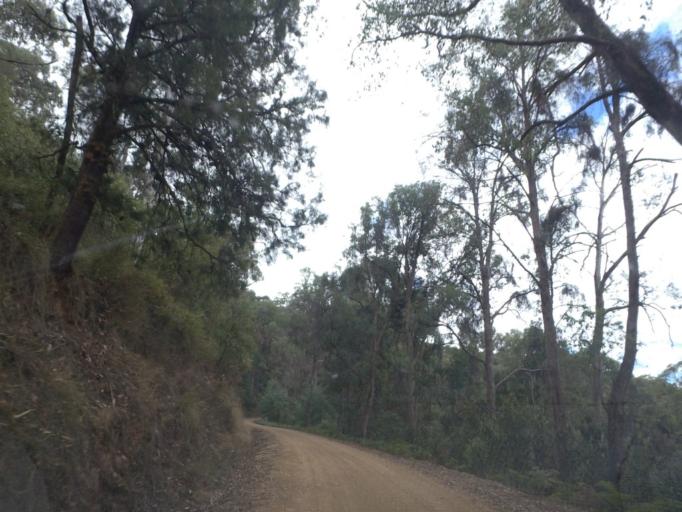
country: AU
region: Victoria
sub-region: Murrindindi
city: Alexandra
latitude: -37.4306
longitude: 145.9727
